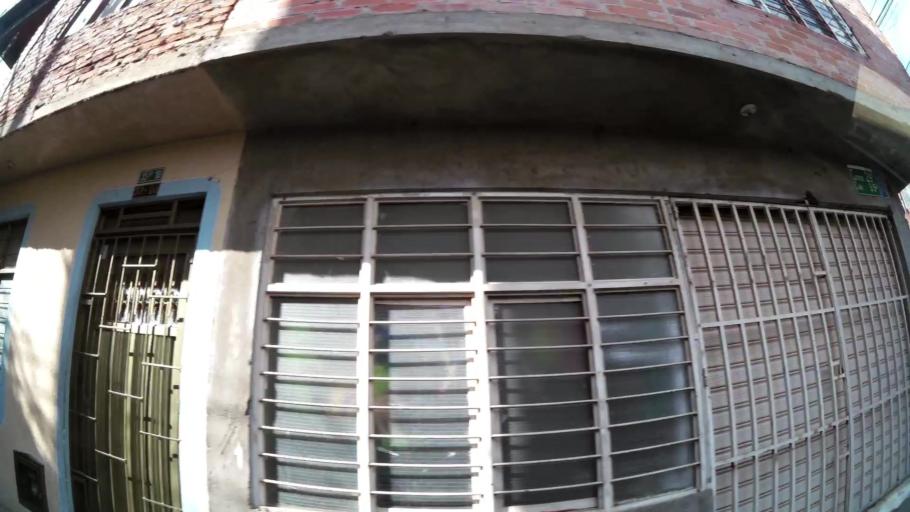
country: CO
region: Valle del Cauca
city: Cali
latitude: 3.4251
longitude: -76.5040
